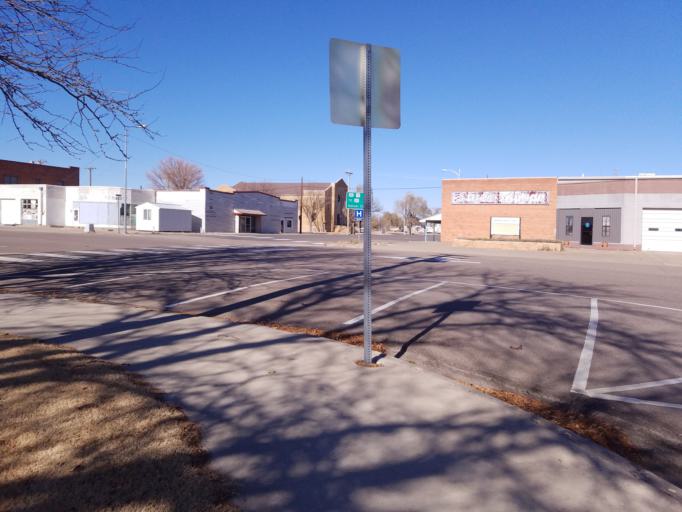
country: US
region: Oklahoma
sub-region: Cimarron County
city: Boise City
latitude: 36.7299
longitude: -102.5128
